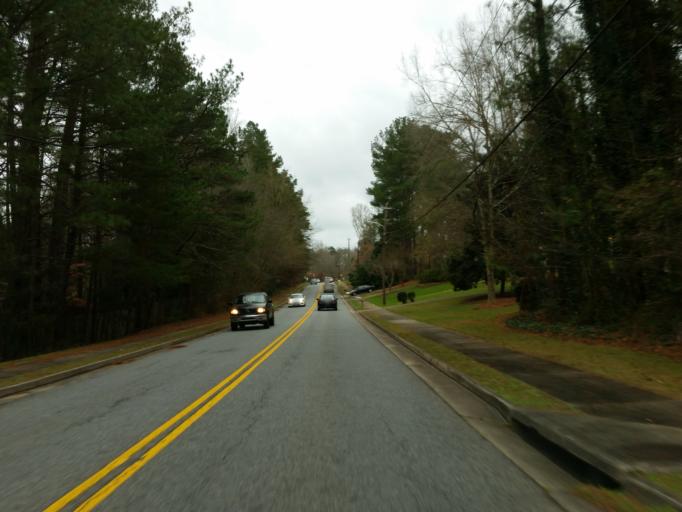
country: US
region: Georgia
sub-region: Cobb County
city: Marietta
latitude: 33.9560
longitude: -84.4649
